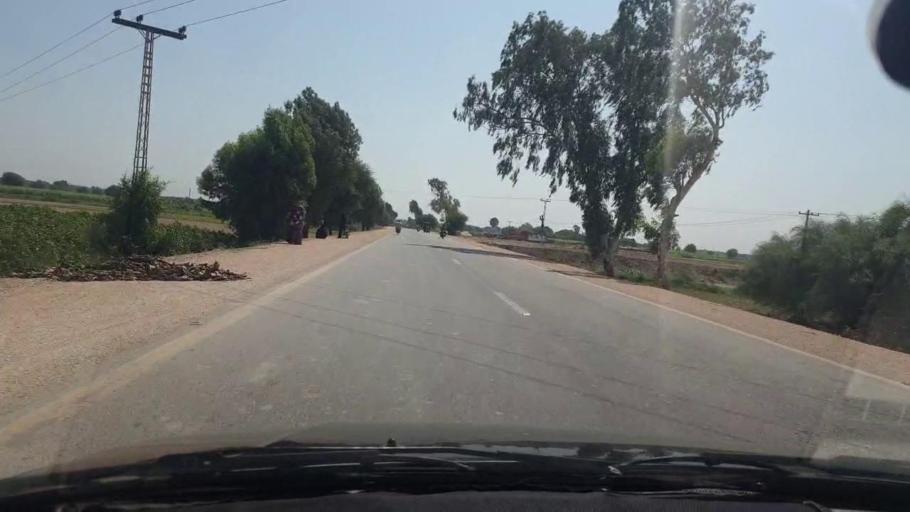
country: PK
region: Sindh
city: Tando Allahyar
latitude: 25.4329
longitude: 68.7454
